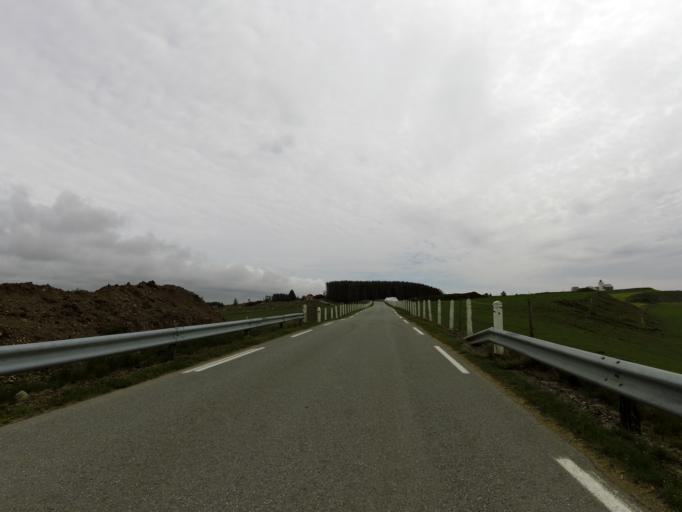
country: NO
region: Rogaland
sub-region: Ha
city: Naerbo
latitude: 58.6633
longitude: 5.5563
